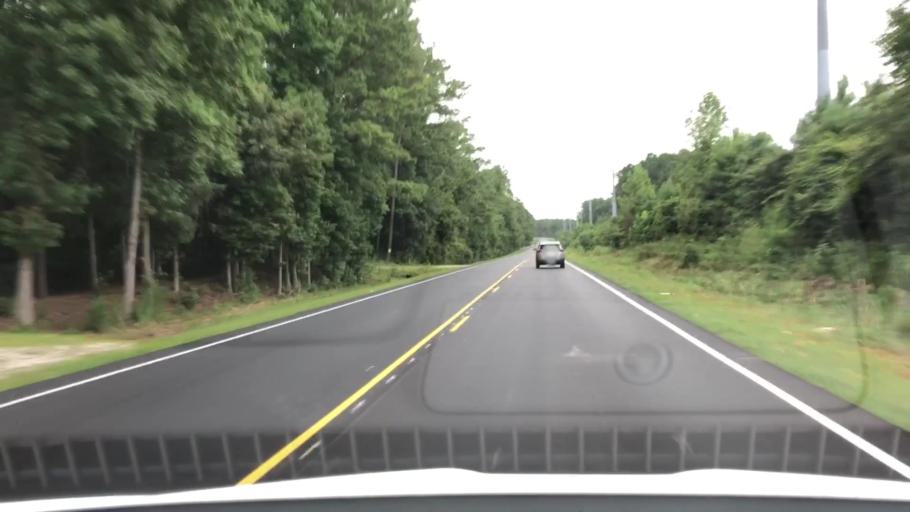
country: US
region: North Carolina
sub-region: Carteret County
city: Cape Carteret
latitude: 34.7624
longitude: -77.0953
